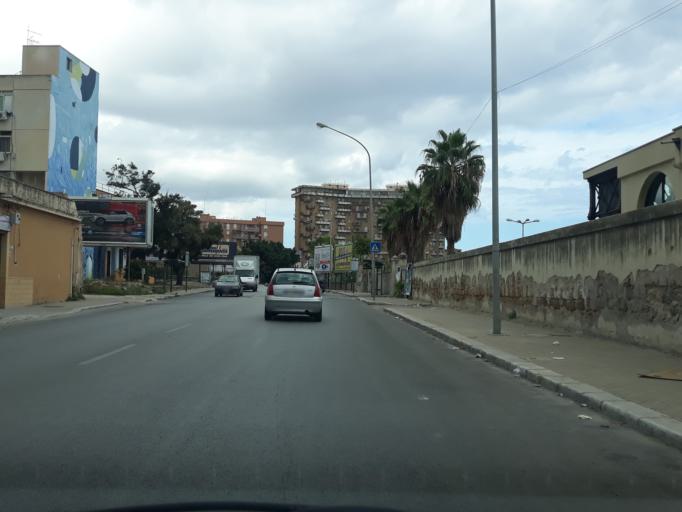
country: IT
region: Sicily
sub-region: Palermo
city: Ciaculli
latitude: 38.1089
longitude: 13.3804
